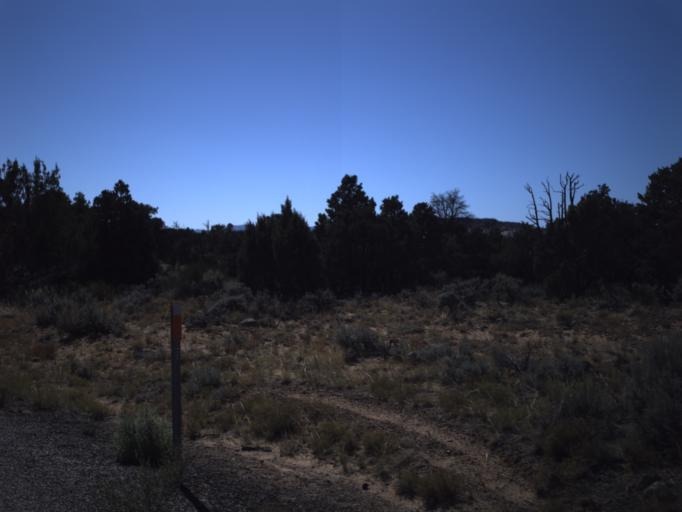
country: US
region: Utah
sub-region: Wayne County
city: Loa
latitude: 37.8641
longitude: -111.4399
